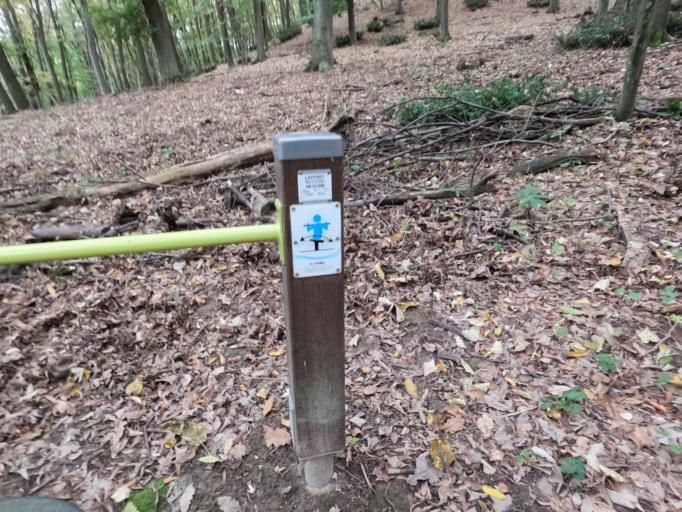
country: HU
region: Tolna
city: Szentgalpuszta
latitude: 46.3275
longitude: 18.6149
